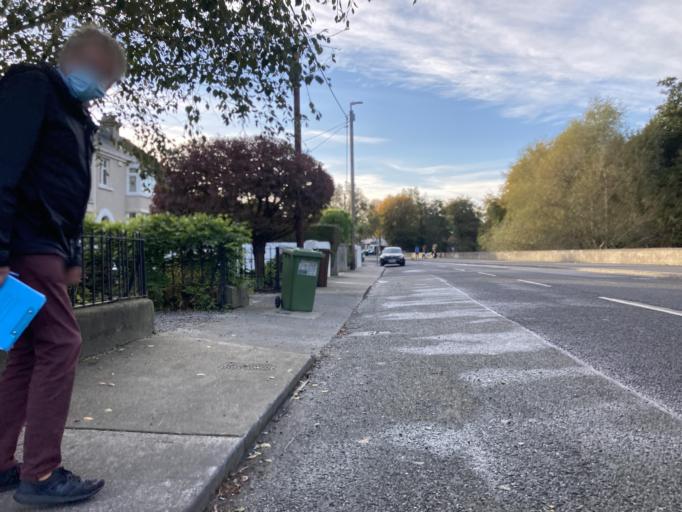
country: IE
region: Leinster
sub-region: South Dublin
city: Terenure
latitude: 53.3048
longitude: -6.2795
